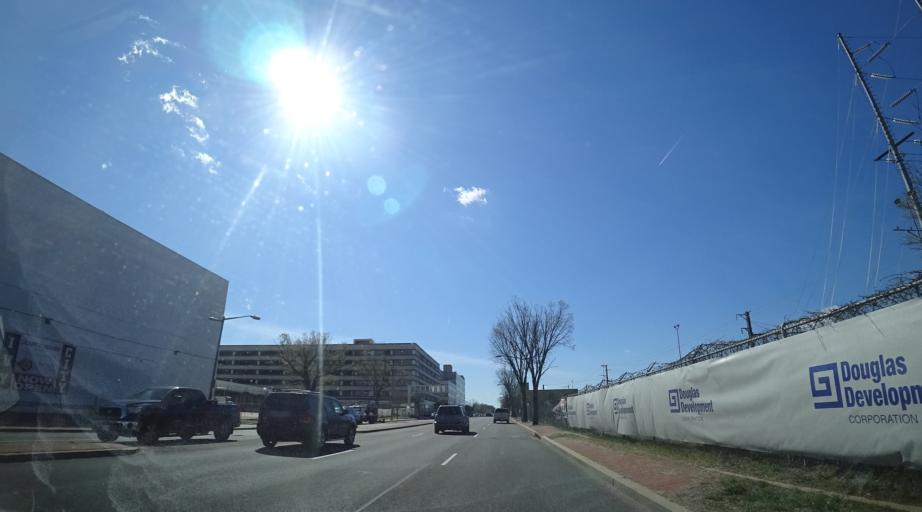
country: US
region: Maryland
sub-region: Prince George's County
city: Mount Rainier
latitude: 38.9170
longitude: -76.9817
